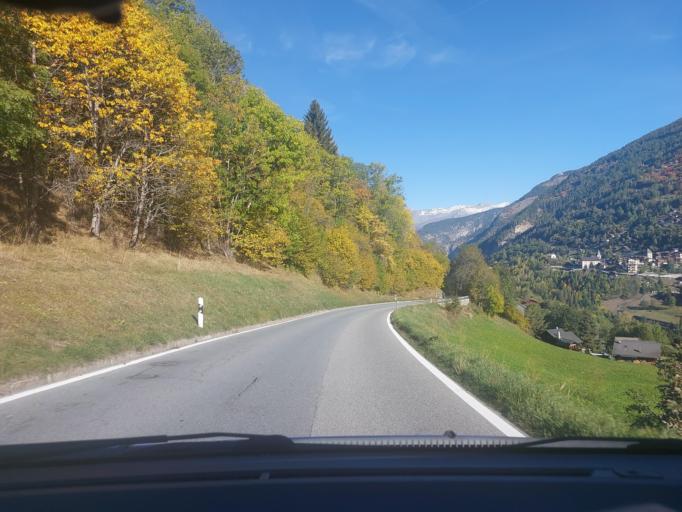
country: CH
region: Valais
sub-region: Sierre District
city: Chippis
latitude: 46.2063
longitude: 7.5833
